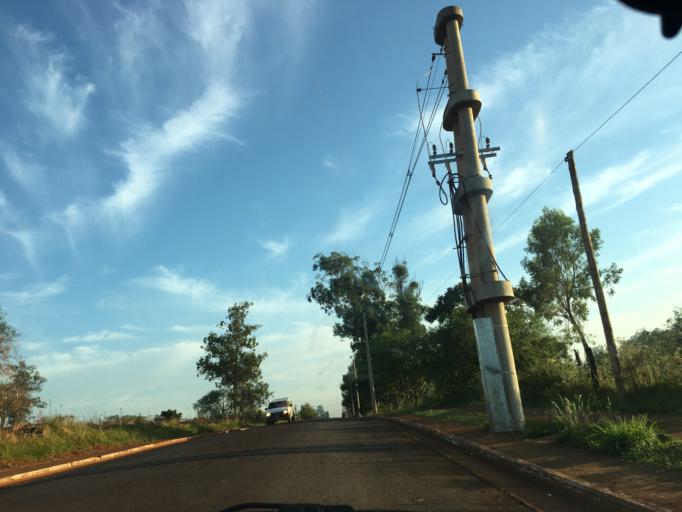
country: AR
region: Misiones
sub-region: Departamento de Capital
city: Posadas
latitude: -27.4500
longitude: -55.9338
